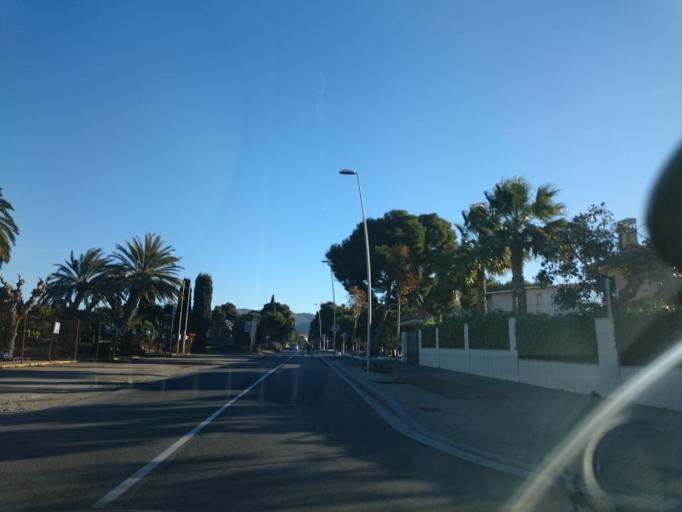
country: ES
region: Catalonia
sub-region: Provincia de Barcelona
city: Sitges
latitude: 41.2332
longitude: 1.7906
